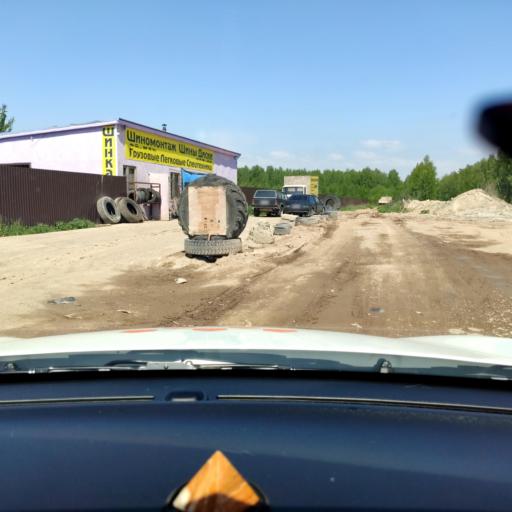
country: RU
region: Tatarstan
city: Stolbishchi
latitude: 55.7041
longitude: 49.1807
